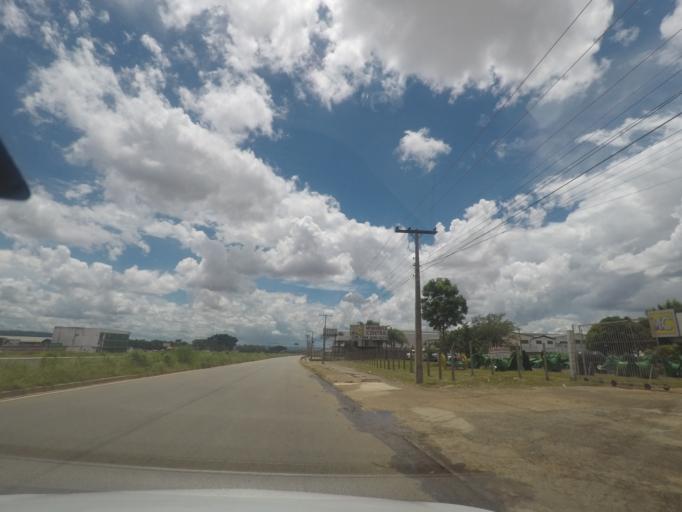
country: BR
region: Goias
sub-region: Goiania
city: Goiania
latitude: -16.7175
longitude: -49.3654
